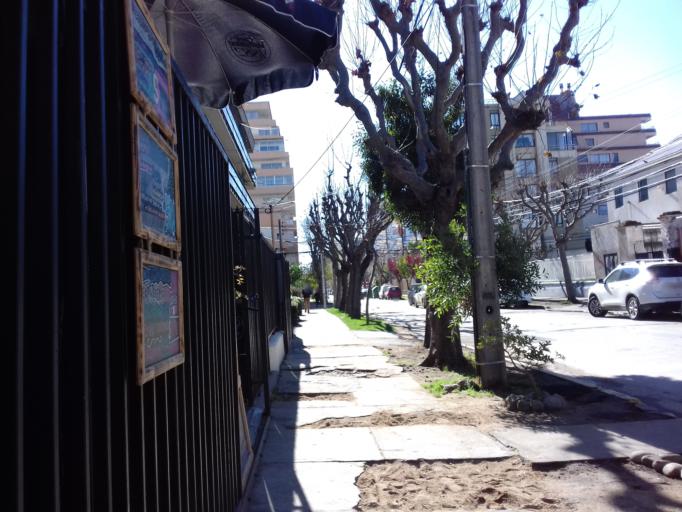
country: CL
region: Valparaiso
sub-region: Provincia de Valparaiso
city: Vina del Mar
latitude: -33.0177
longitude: -71.5519
